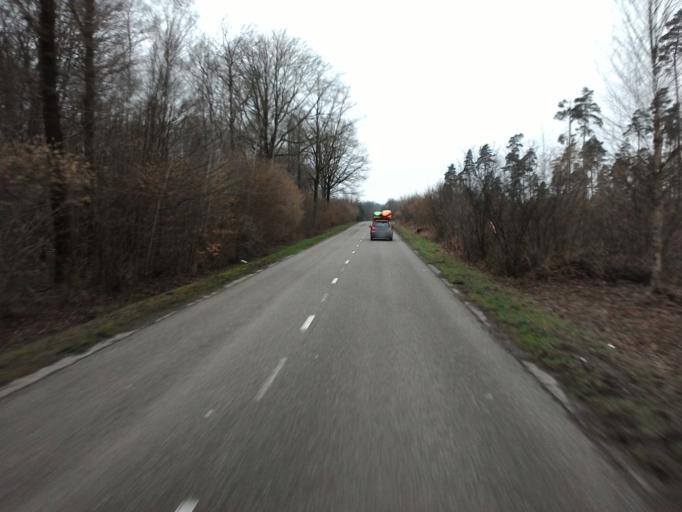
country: BE
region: Wallonia
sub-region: Province de Namur
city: Beauraing
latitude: 50.0437
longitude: 4.9666
